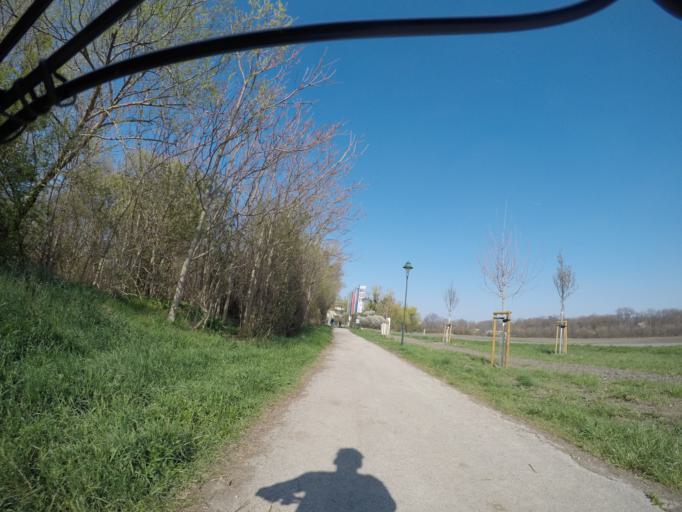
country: AT
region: Lower Austria
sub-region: Politischer Bezirk Modling
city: Laxenburg
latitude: 48.0624
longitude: 16.3492
